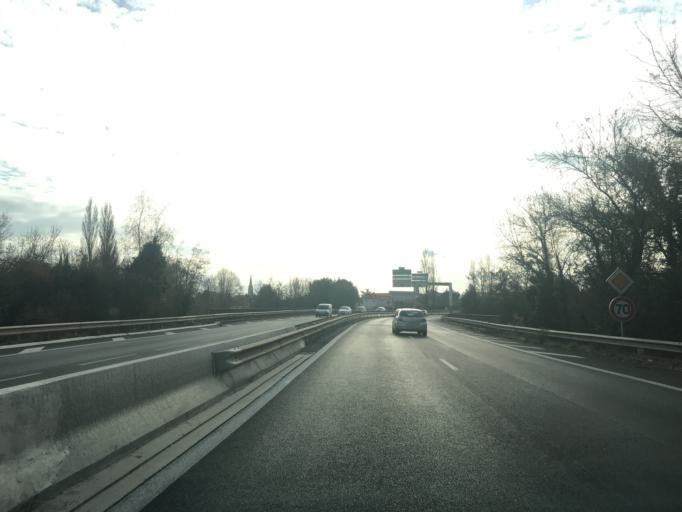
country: FR
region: Poitou-Charentes
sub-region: Departement des Deux-Sevres
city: Niort
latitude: 46.3355
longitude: -0.4652
